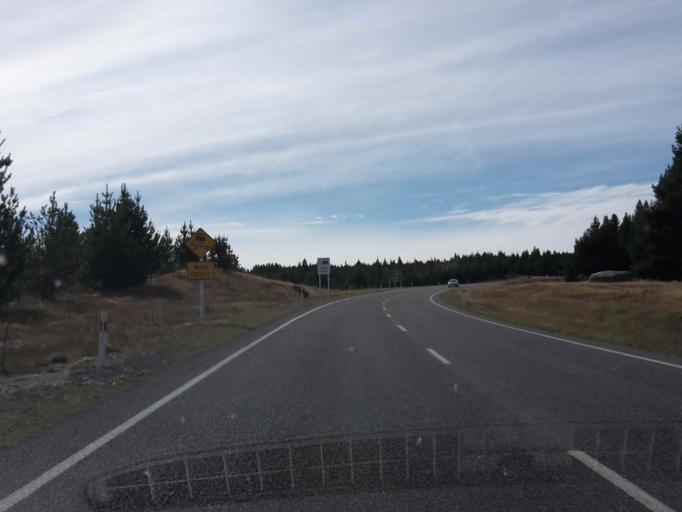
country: NZ
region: Canterbury
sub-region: Timaru District
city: Pleasant Point
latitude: -44.1909
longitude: 170.1220
